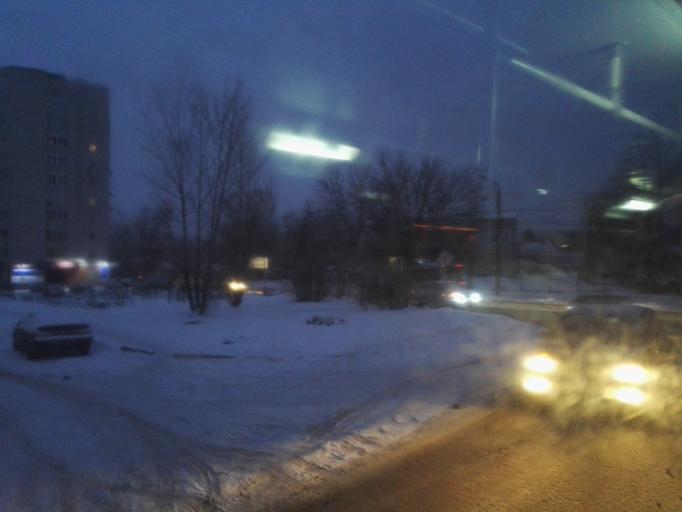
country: RU
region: Tula
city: Mendeleyevskiy
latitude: 54.1626
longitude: 37.5993
